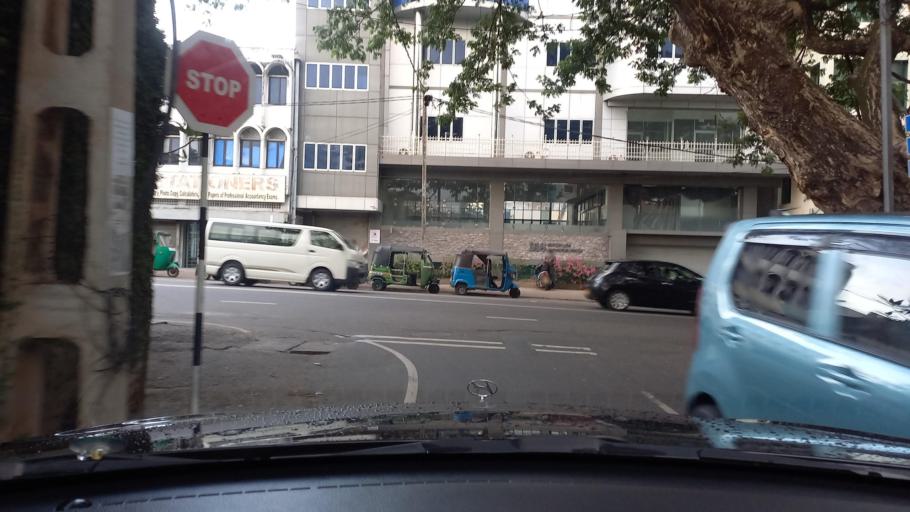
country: LK
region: Western
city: Pita Kotte
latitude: 6.8786
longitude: 79.8696
